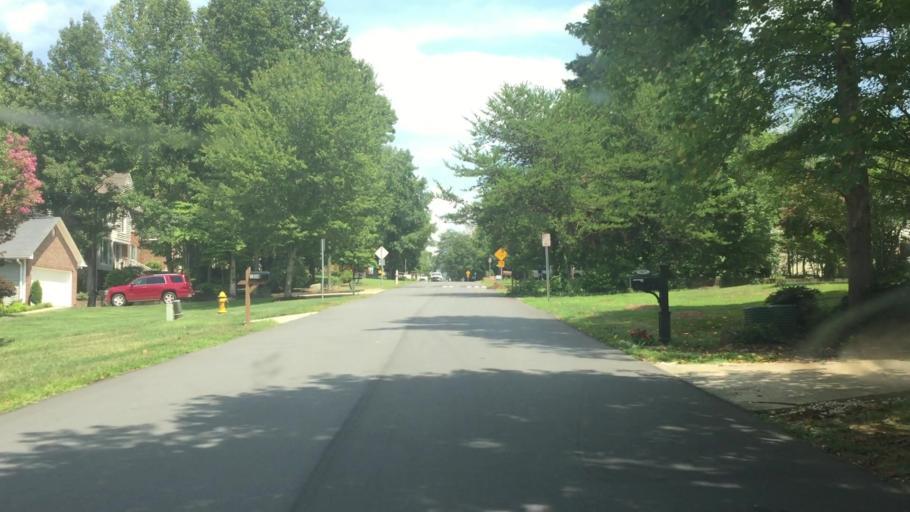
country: US
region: North Carolina
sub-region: Iredell County
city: Mooresville
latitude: 35.5517
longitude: -80.7944
